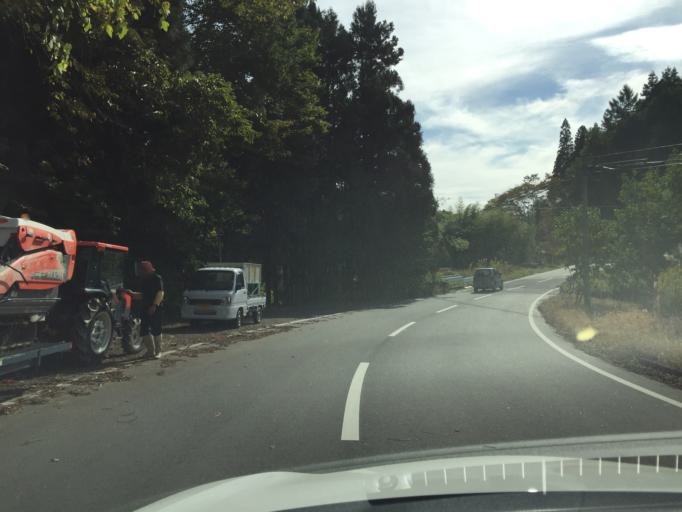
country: JP
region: Fukushima
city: Nihommatsu
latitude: 37.5316
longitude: 140.5074
